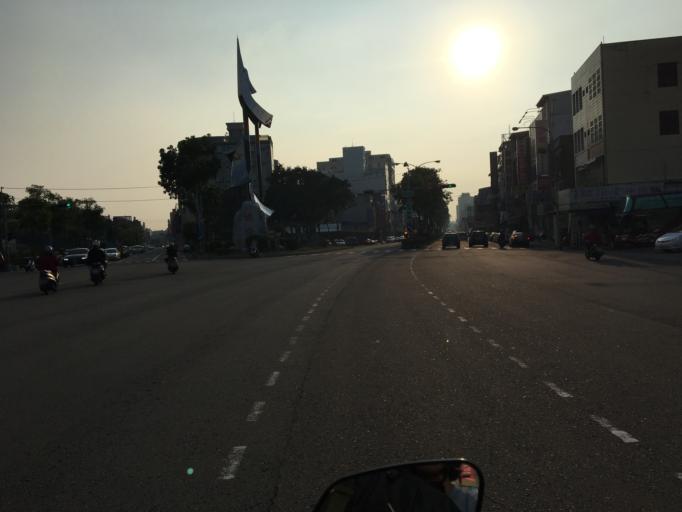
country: TW
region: Taiwan
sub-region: Hsinchu
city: Hsinchu
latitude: 24.6905
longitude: 120.9130
